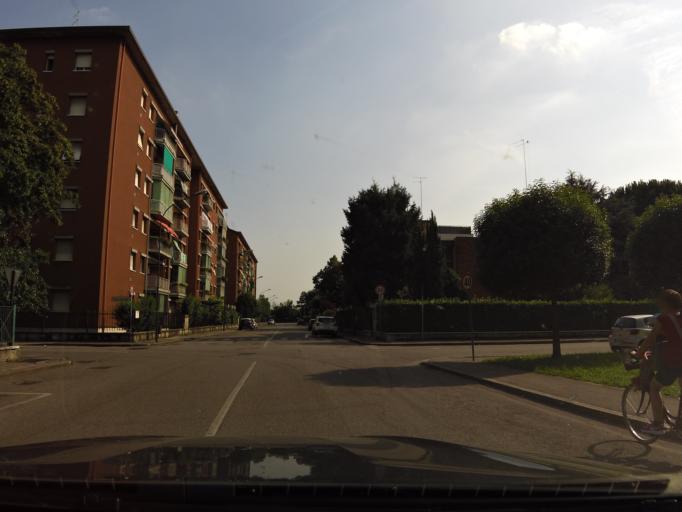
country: IT
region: Veneto
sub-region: Provincia di Verona
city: Verona
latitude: 45.4426
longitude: 10.9631
